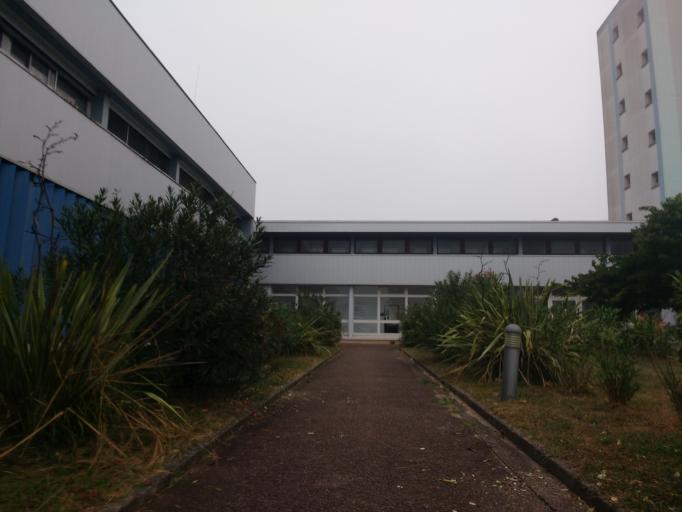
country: FR
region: Aquitaine
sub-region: Departement de la Gironde
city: Talence
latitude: 44.8045
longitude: -0.6020
